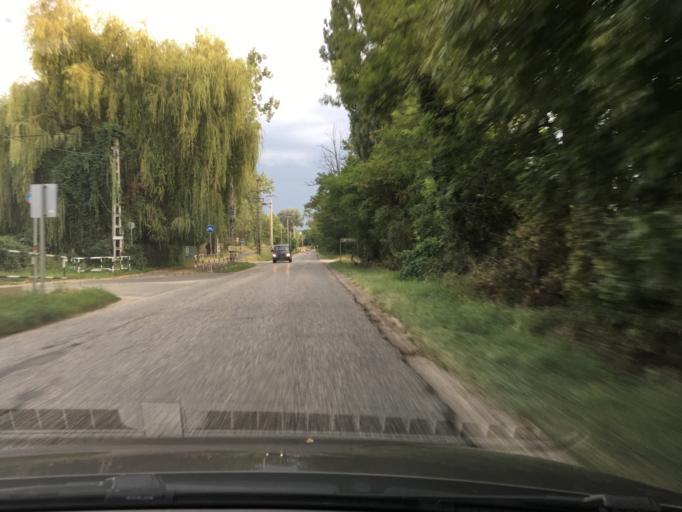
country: HU
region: Pest
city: Szada
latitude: 47.6253
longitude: 19.3008
